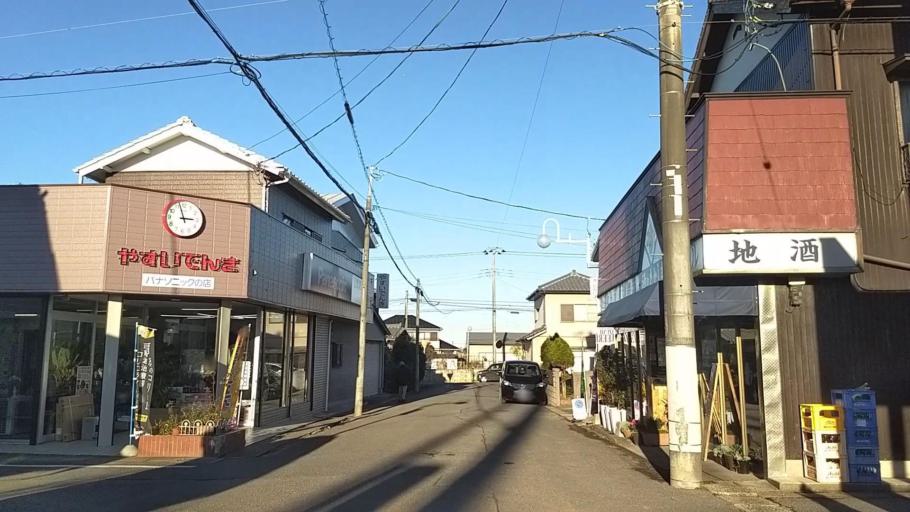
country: JP
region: Chiba
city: Hasaki
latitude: 35.7657
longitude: 140.7591
